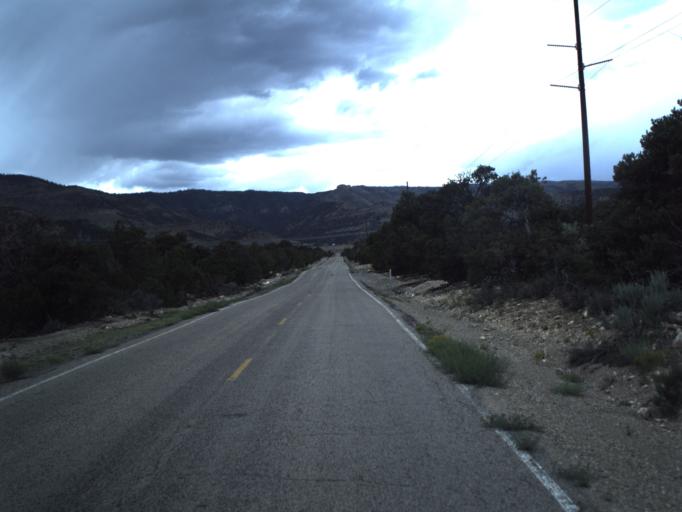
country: US
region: Utah
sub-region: Emery County
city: Huntington
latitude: 39.4842
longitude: -110.9736
